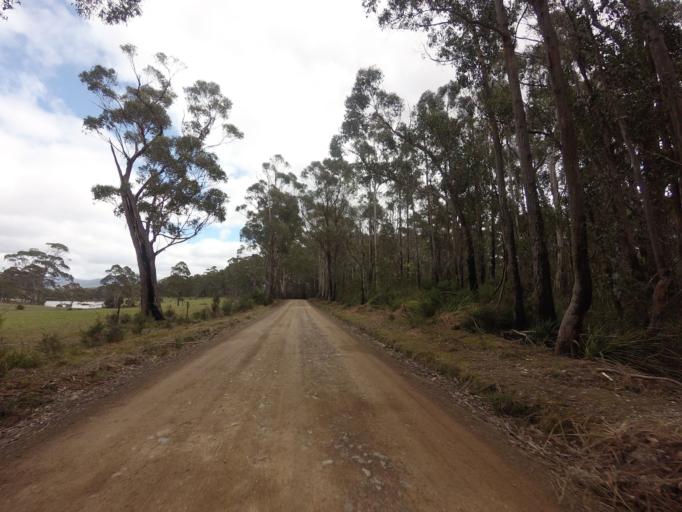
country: AU
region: Tasmania
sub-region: Huon Valley
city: Geeveston
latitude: -43.4256
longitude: 147.0010
